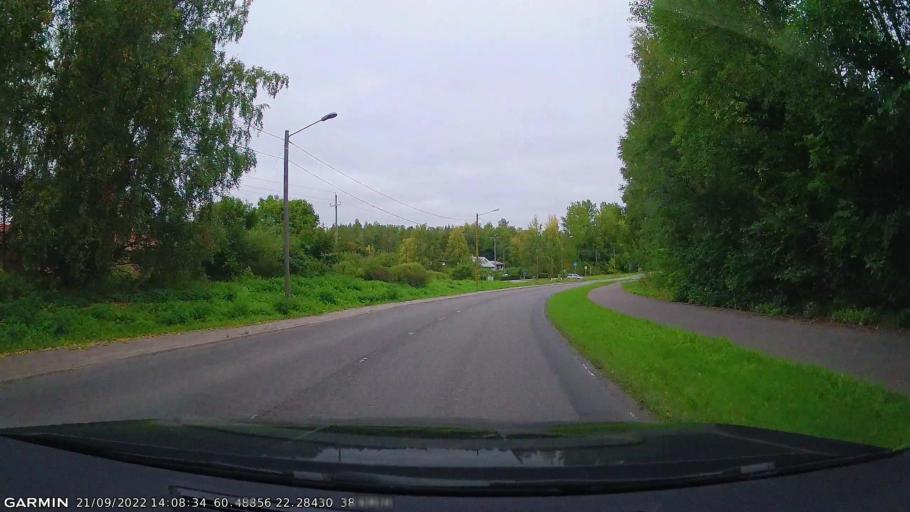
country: FI
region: Varsinais-Suomi
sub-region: Turku
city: Turku
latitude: 60.4886
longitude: 22.2843
